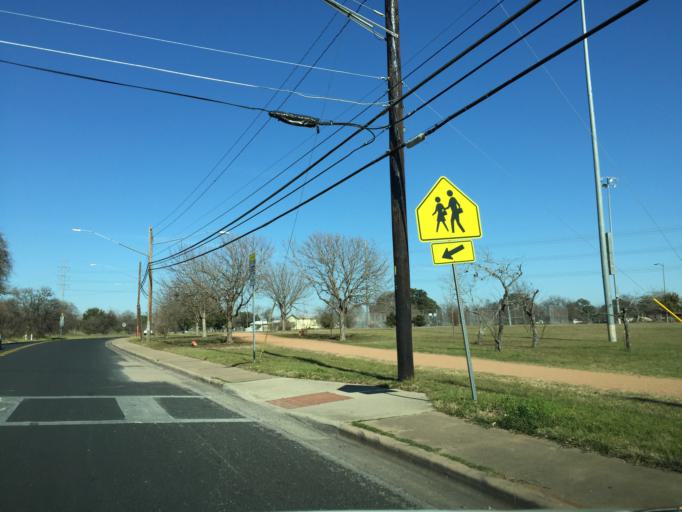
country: US
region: Texas
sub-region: Travis County
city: Austin
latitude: 30.2373
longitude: -97.6912
